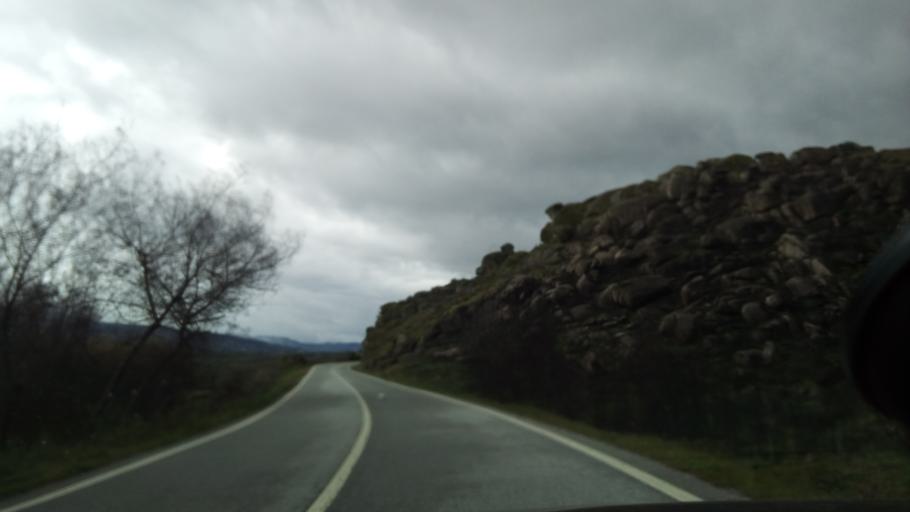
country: PT
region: Guarda
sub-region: Fornos de Algodres
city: Fornos de Algodres
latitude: 40.5611
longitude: -7.5606
